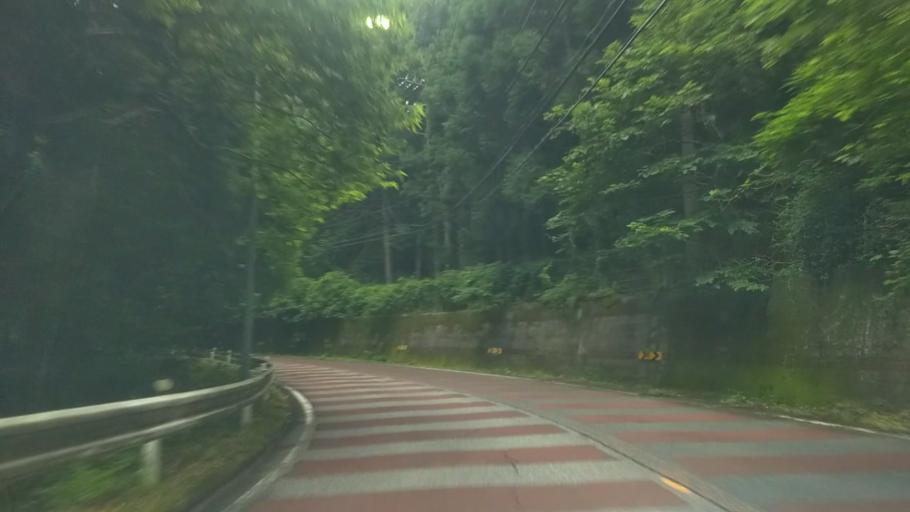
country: JP
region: Chiba
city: Kawaguchi
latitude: 35.2080
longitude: 140.0672
